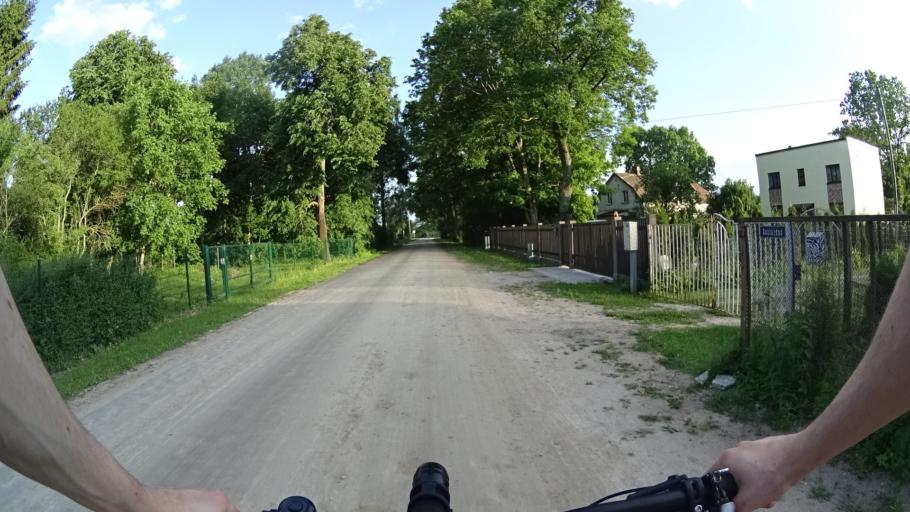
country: LV
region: Riga
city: Jaunciems
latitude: 57.1024
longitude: 24.1941
